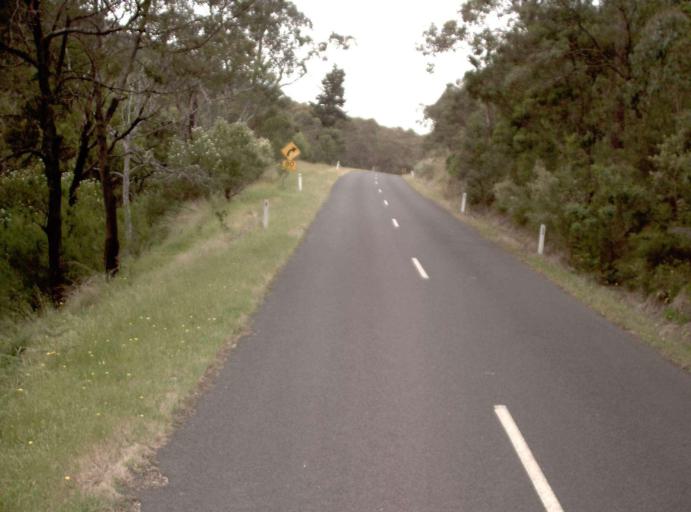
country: AU
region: Victoria
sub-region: East Gippsland
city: Bairnsdale
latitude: -37.4769
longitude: 147.2130
